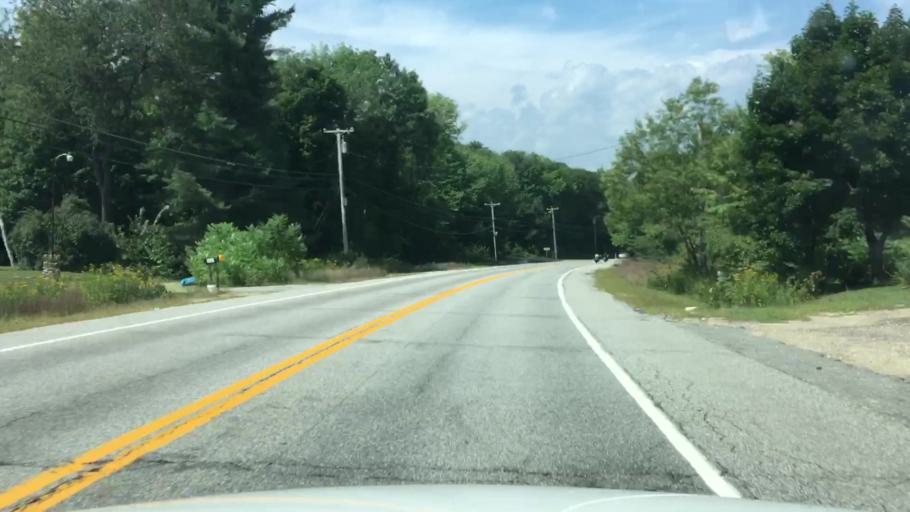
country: US
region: Maine
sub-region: Oxford County
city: Peru
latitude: 44.5007
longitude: -70.3987
